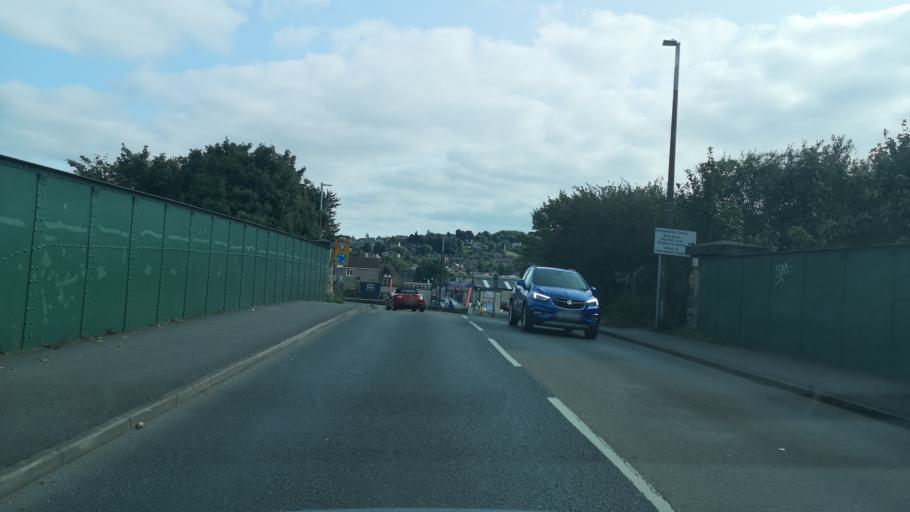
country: GB
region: England
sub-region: Kirklees
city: Dewsbury
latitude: 53.6765
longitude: -1.6354
